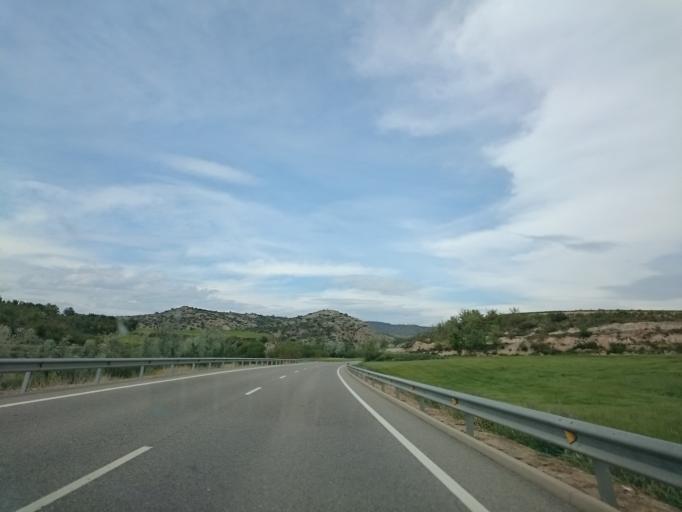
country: ES
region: Catalonia
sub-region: Provincia de Lleida
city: Tora de Riubregos
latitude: 41.8208
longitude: 1.3248
